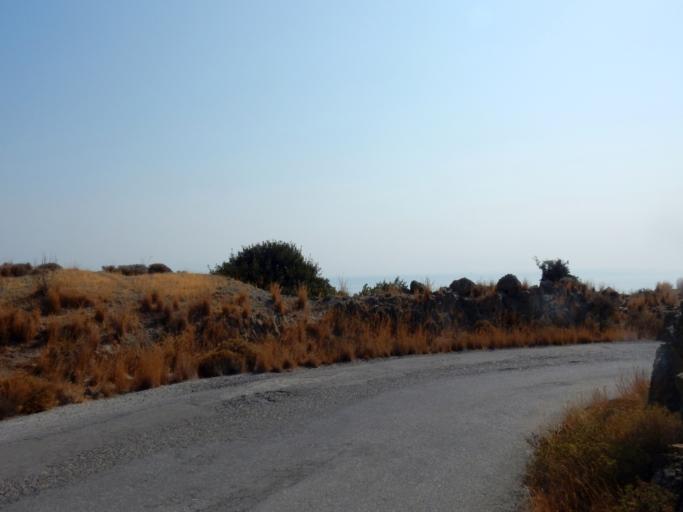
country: GR
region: Attica
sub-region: Nomos Piraios
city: Vathi
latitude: 37.7297
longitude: 23.5346
